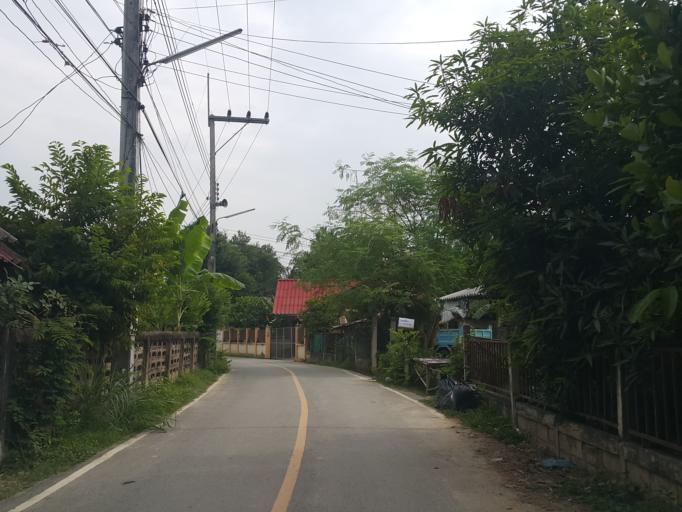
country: TH
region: Chiang Mai
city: San Sai
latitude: 18.8023
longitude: 99.0743
